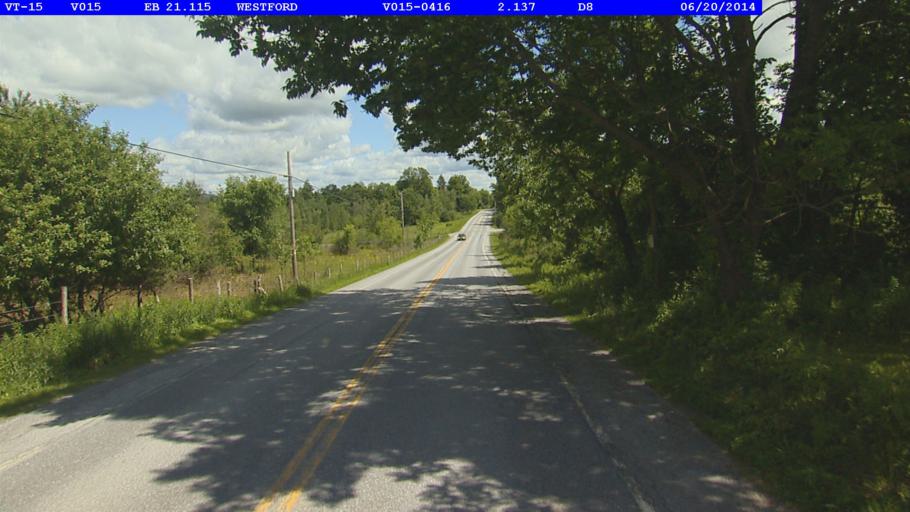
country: US
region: Vermont
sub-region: Chittenden County
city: Jericho
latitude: 44.6237
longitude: -72.9235
